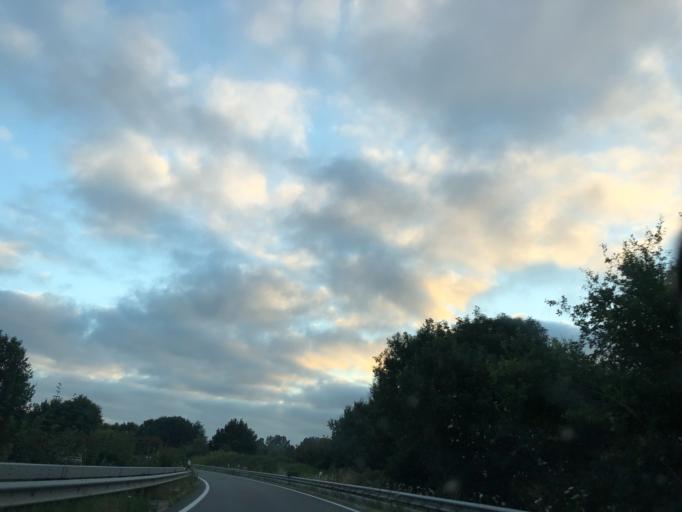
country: DE
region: Lower Saxony
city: Bunde
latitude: 53.1637
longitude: 7.2855
